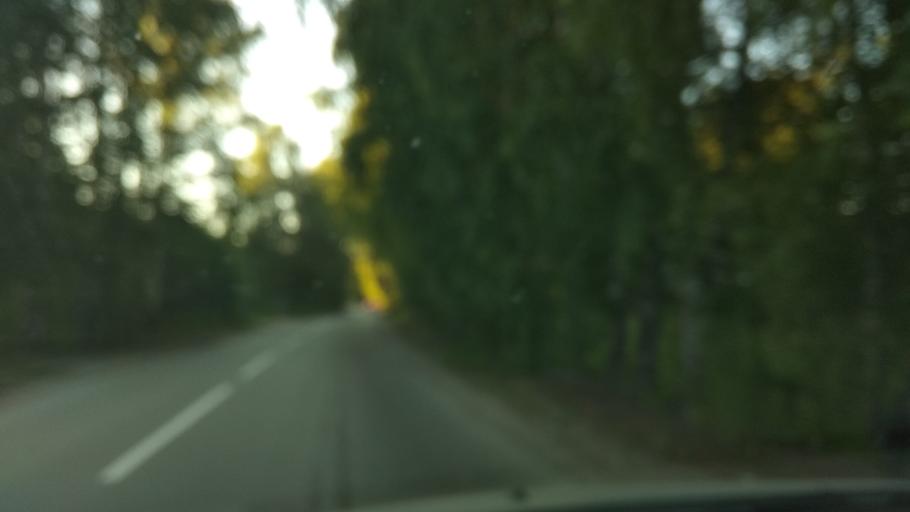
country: RU
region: Sverdlovsk
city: Sredneuralsk
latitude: 56.9811
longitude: 60.4608
